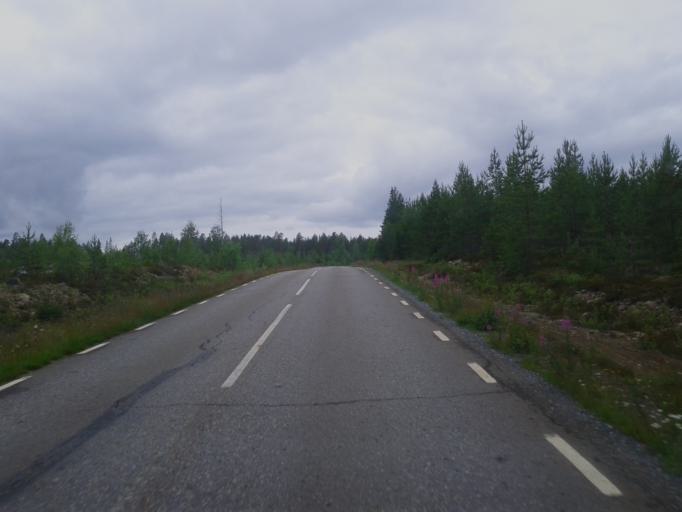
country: SE
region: Vaesterbotten
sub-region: Skelleftea Kommun
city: Kage
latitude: 64.9179
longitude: 20.9138
